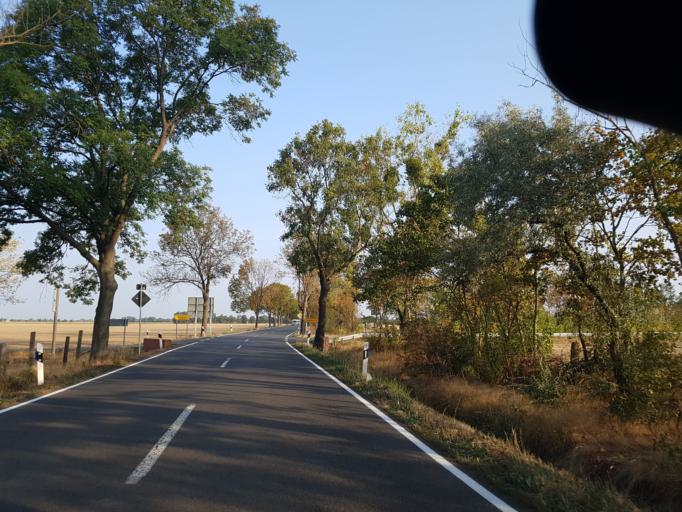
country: DE
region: Saxony-Anhalt
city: Muhlanger
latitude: 51.7865
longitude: 12.7098
